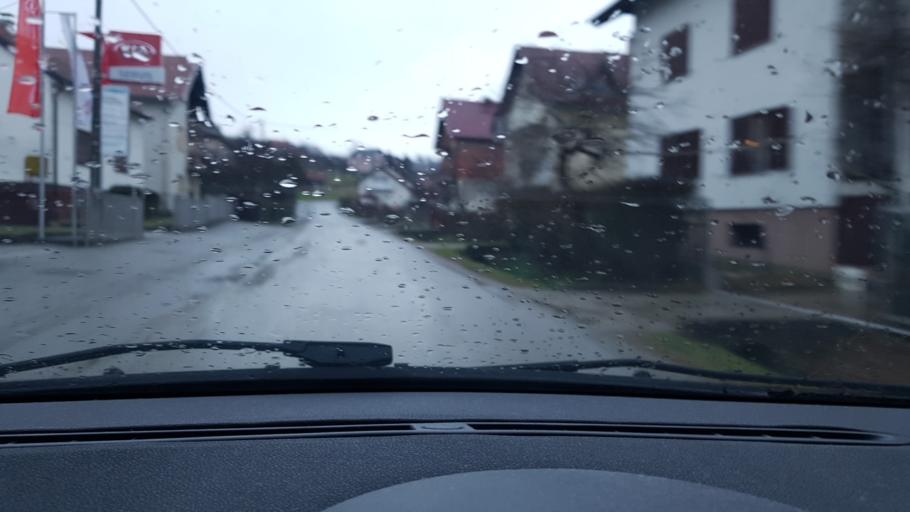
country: HR
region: Krapinsko-Zagorska
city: Bedekovcina
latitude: 45.9868
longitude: 15.9774
